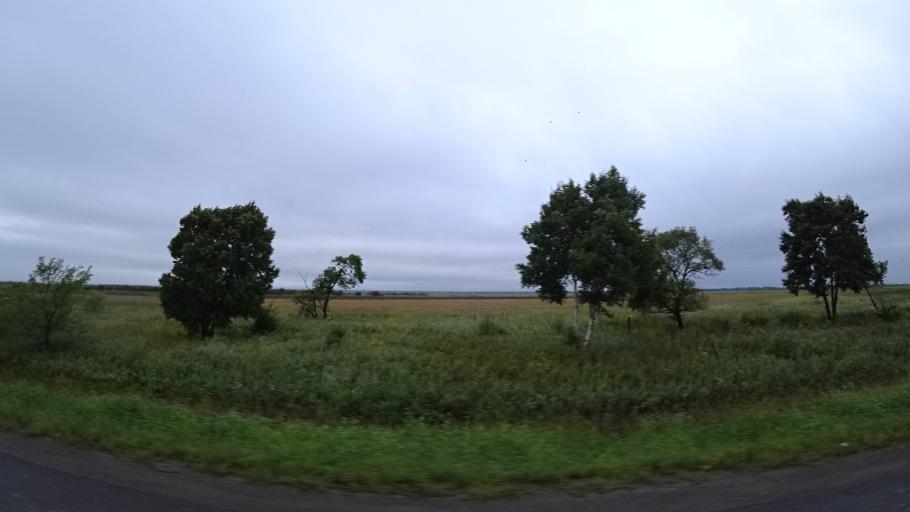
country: RU
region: Primorskiy
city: Chernigovka
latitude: 44.2968
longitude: 132.5206
